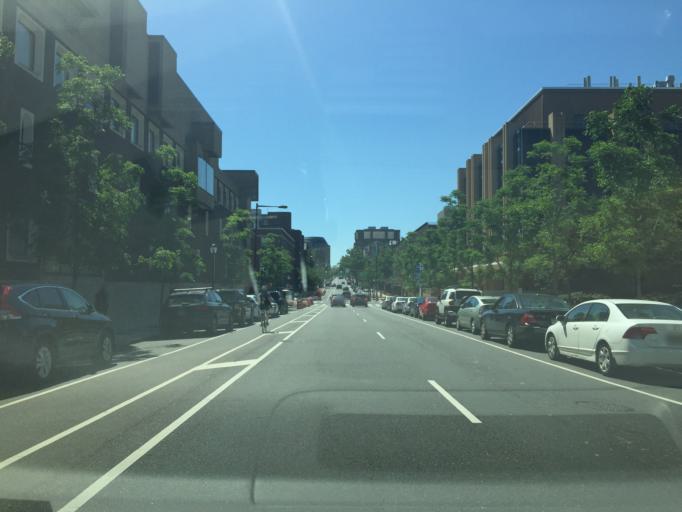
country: US
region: Pennsylvania
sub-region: Philadelphia County
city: Philadelphia
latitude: 39.9524
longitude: -75.1889
